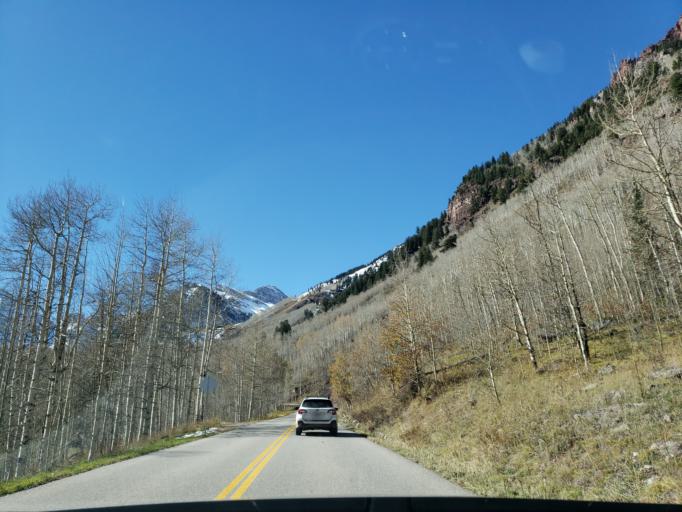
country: US
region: Colorado
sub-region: Pitkin County
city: Snowmass Village
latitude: 39.1050
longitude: -106.9300
